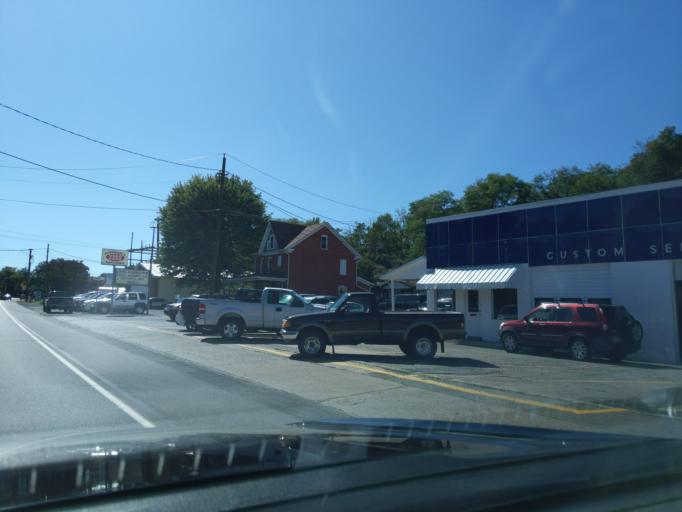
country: US
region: Pennsylvania
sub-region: Blair County
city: Greenwood
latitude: 40.5329
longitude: -78.3602
